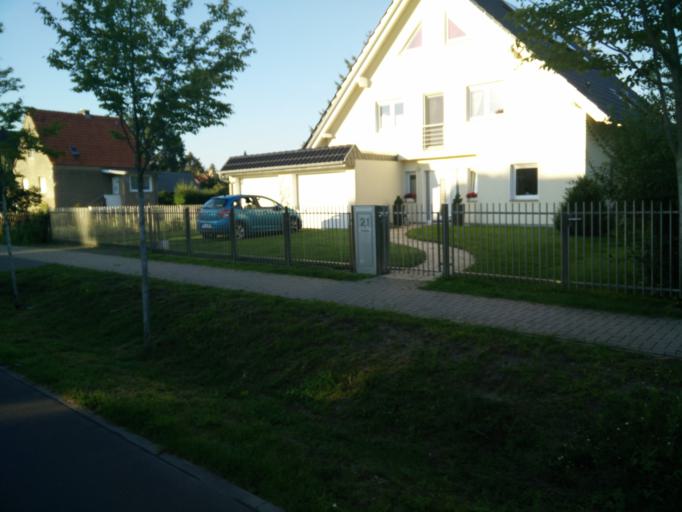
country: DE
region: Brandenburg
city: Falkensee
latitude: 52.5686
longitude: 13.0927
